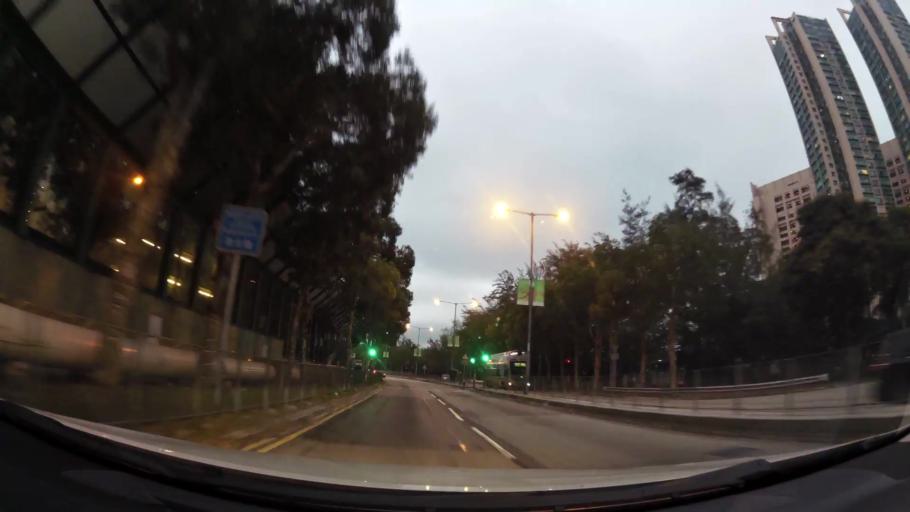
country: HK
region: Tsuen Wan
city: Tsuen Wan
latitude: 22.3440
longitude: 114.1092
